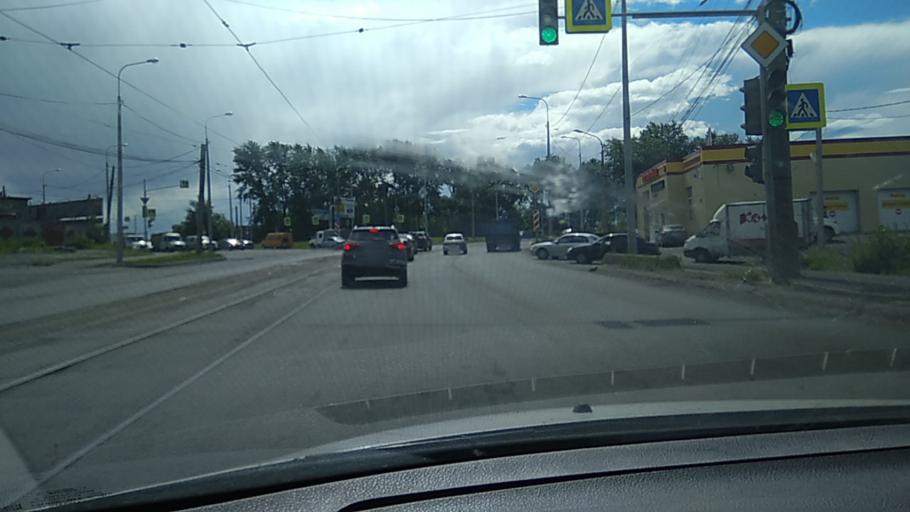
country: RU
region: Sverdlovsk
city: Nizhniy Tagil
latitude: 57.9224
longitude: 59.9887
